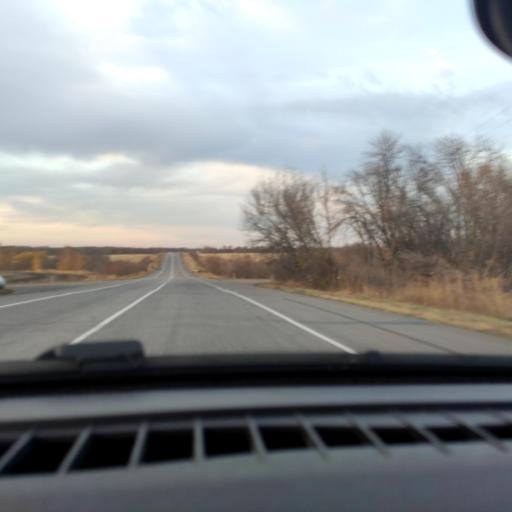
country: RU
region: Voronezj
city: Devitsa
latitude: 51.5711
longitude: 38.9747
